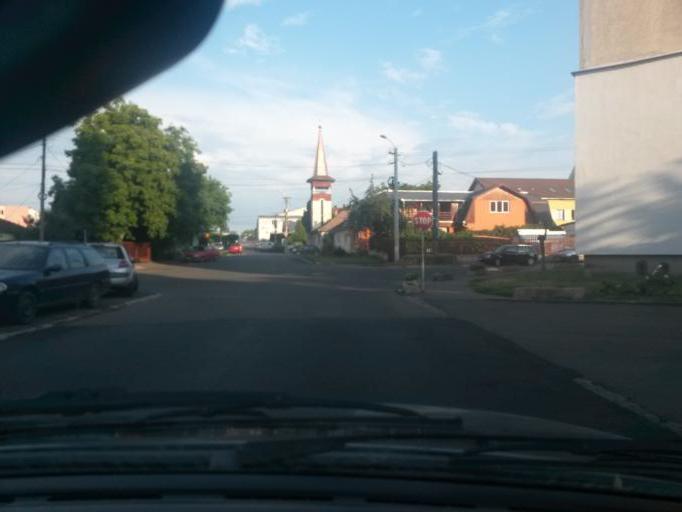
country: RO
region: Mures
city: Targu-Mures
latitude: 46.5332
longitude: 24.5826
